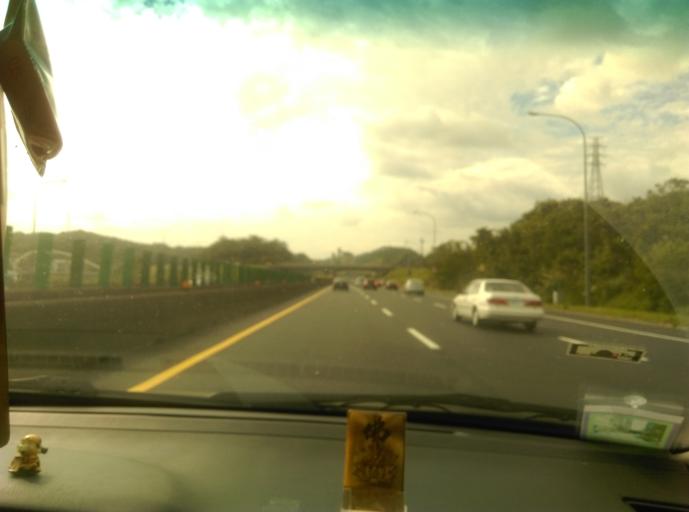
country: TW
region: Taiwan
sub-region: Keelung
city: Keelung
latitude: 25.0874
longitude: 121.6899
